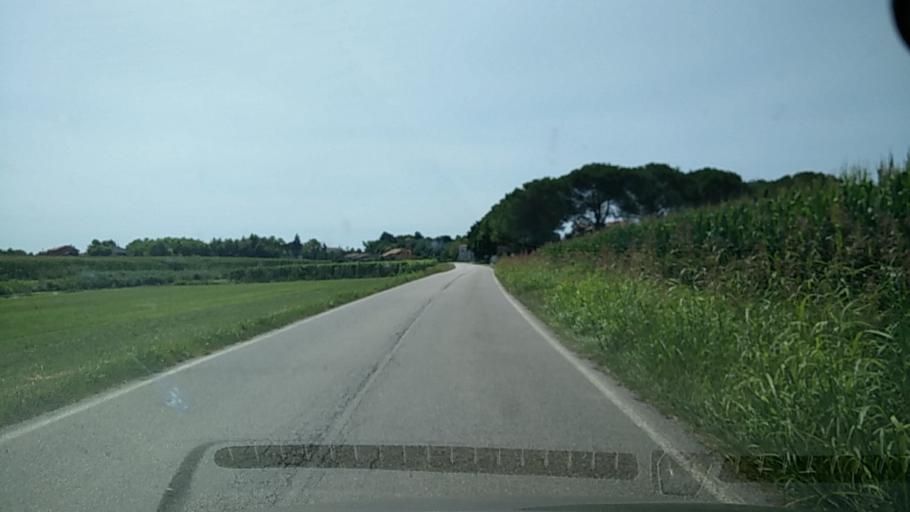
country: IT
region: Veneto
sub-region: Provincia di Treviso
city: Chiarano
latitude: 45.7161
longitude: 12.5872
